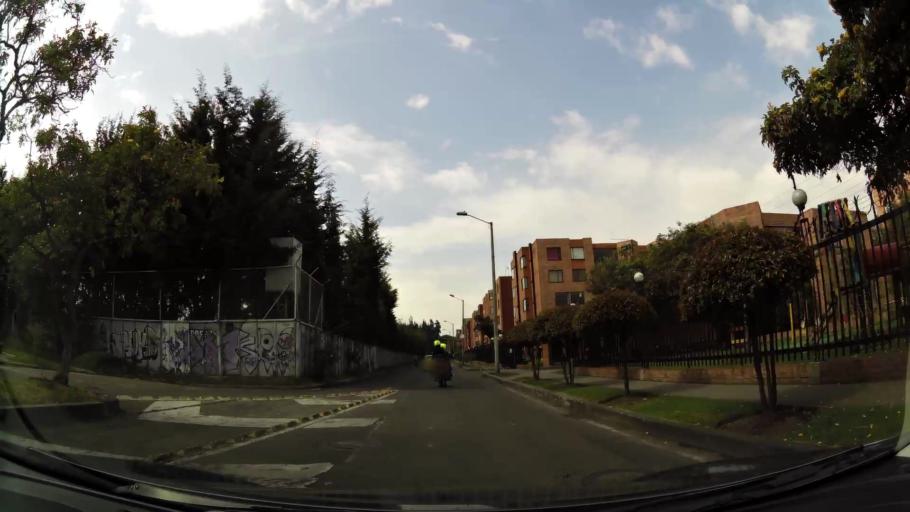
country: CO
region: Bogota D.C.
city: Barrio San Luis
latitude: 4.7359
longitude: -74.0524
